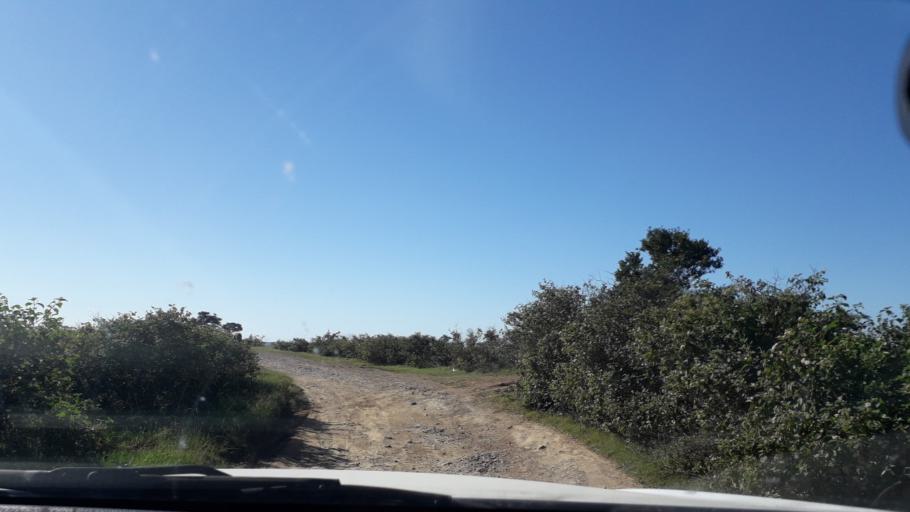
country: ZA
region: Eastern Cape
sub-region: Buffalo City Metropolitan Municipality
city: East London
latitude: -32.8415
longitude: 27.9827
